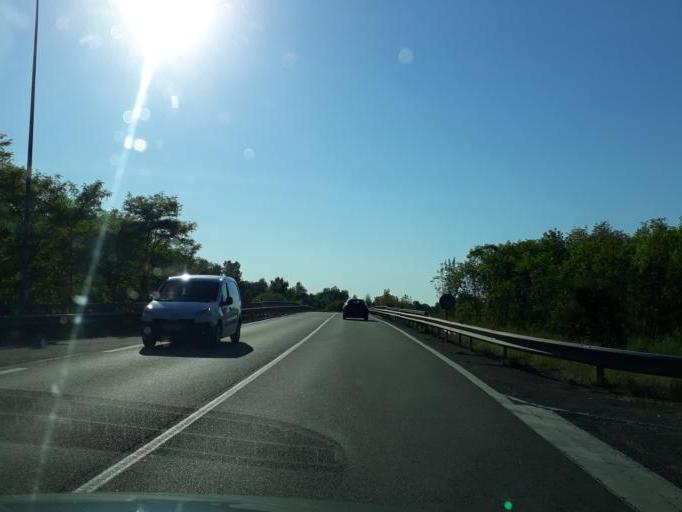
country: FR
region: Bourgogne
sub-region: Departement de la Nievre
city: Neuvy-sur-Loire
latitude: 47.5141
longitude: 2.8891
